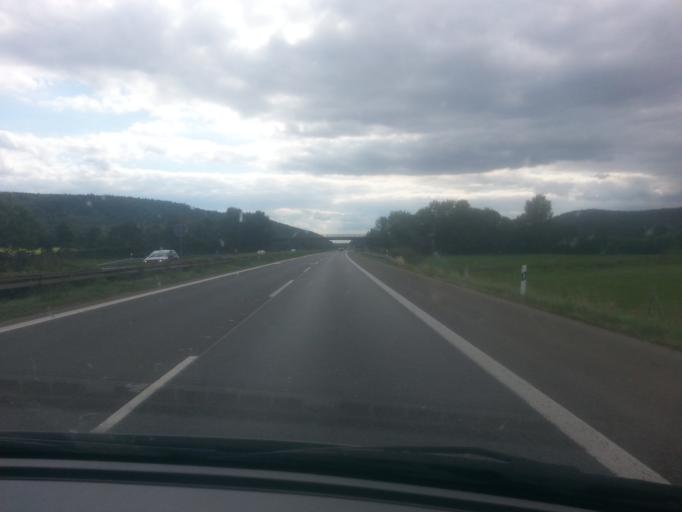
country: DE
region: Bavaria
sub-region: Upper Palatinate
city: Nabburg
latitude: 49.4398
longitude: 12.1852
